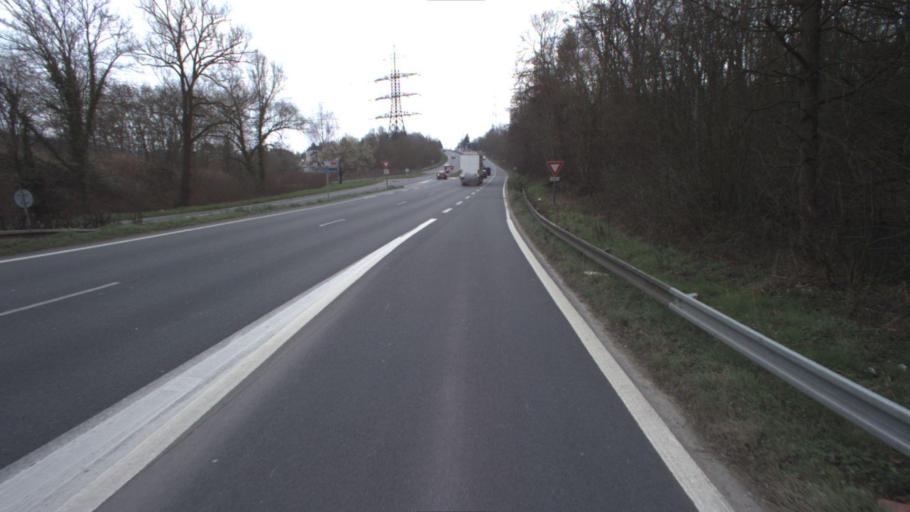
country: FR
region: Ile-de-France
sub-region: Departement de l'Essonne
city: Igny
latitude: 48.7476
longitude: 2.2185
